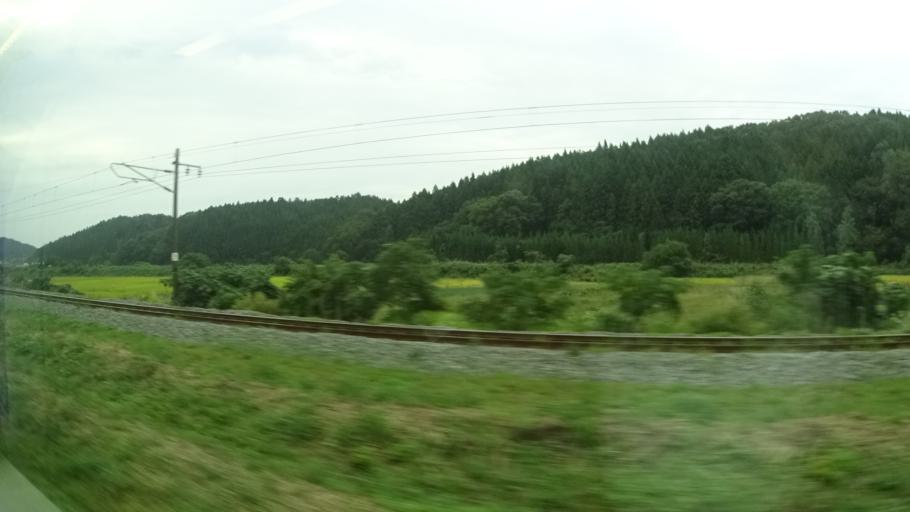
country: JP
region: Yamagata
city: Tsuruoka
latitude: 38.7007
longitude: 139.6816
